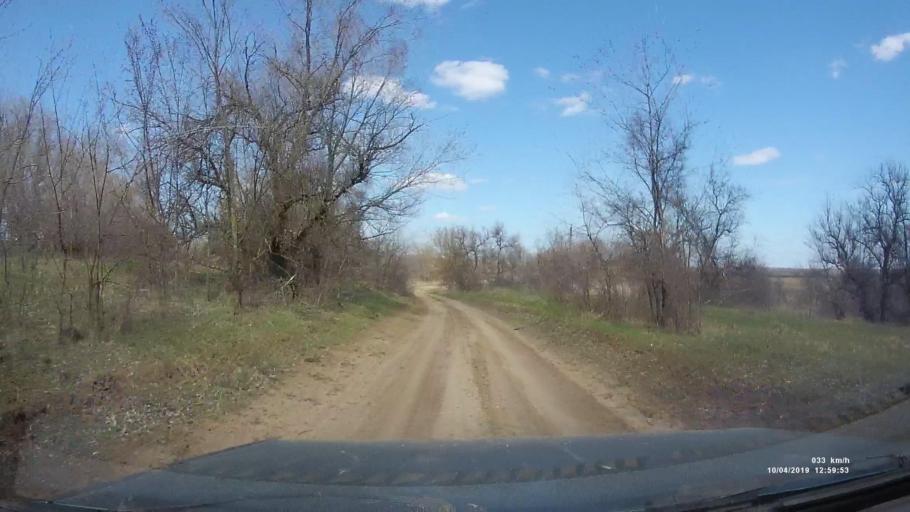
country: RU
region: Rostov
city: Masalovka
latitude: 48.3792
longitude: 40.2292
